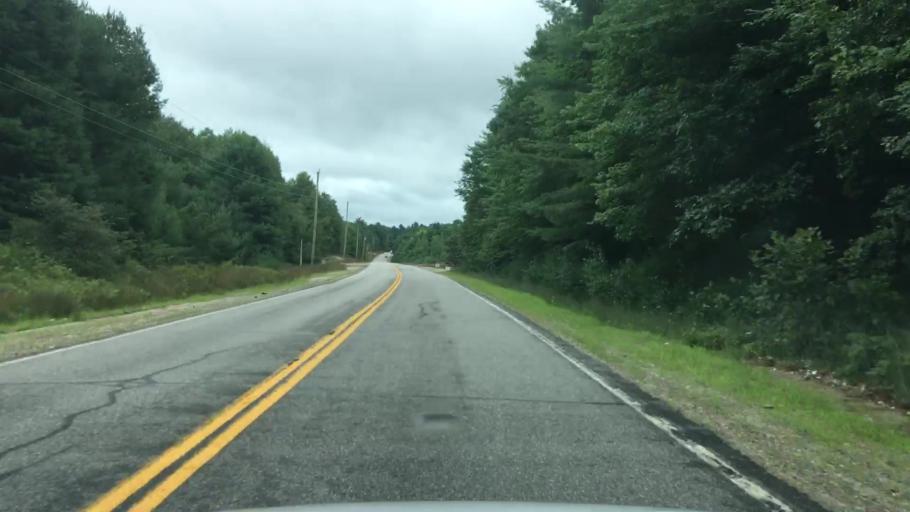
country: US
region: Maine
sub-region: Oxford County
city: Hiram
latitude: 43.9001
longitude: -70.8361
